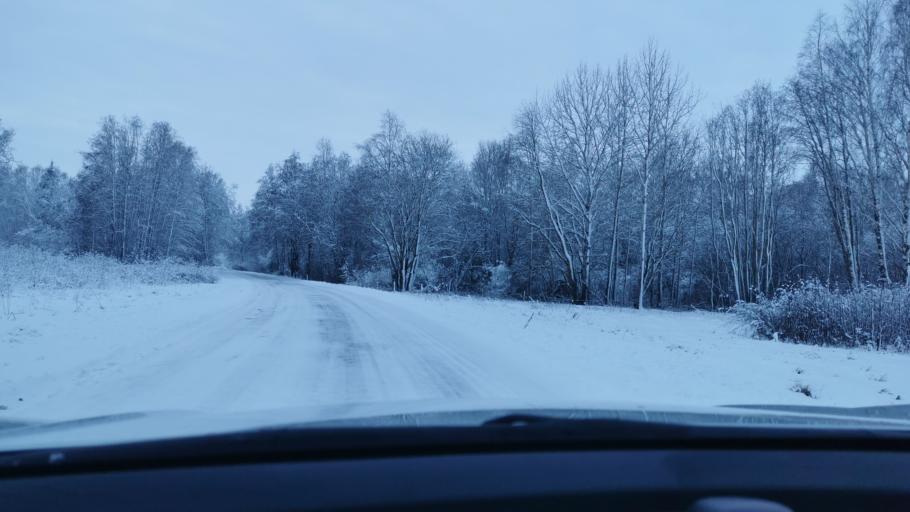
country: EE
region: Laeaene-Virumaa
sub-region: Viru-Nigula vald
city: Kunda
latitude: 59.4453
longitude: 26.5066
